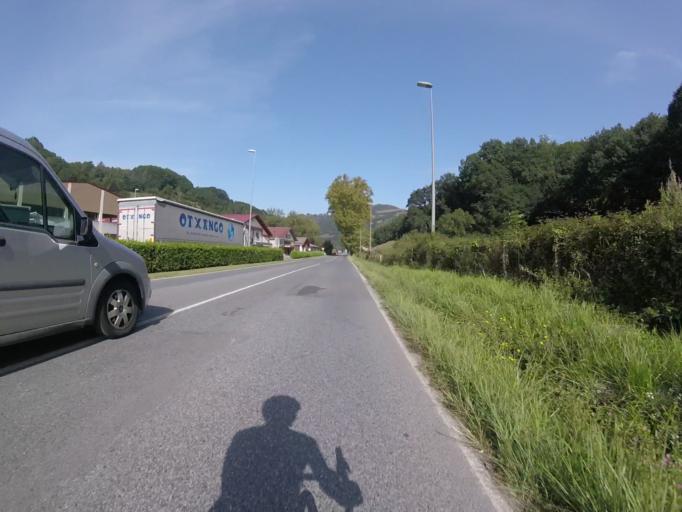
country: ES
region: Navarre
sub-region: Provincia de Navarra
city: Doneztebe
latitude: 43.1330
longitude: -1.5516
